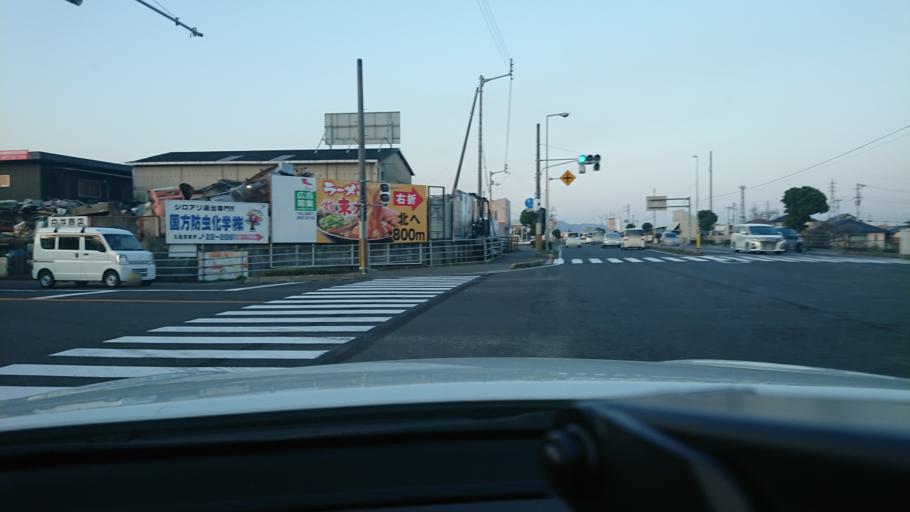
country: JP
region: Kagawa
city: Marugame
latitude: 34.2799
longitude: 133.8165
